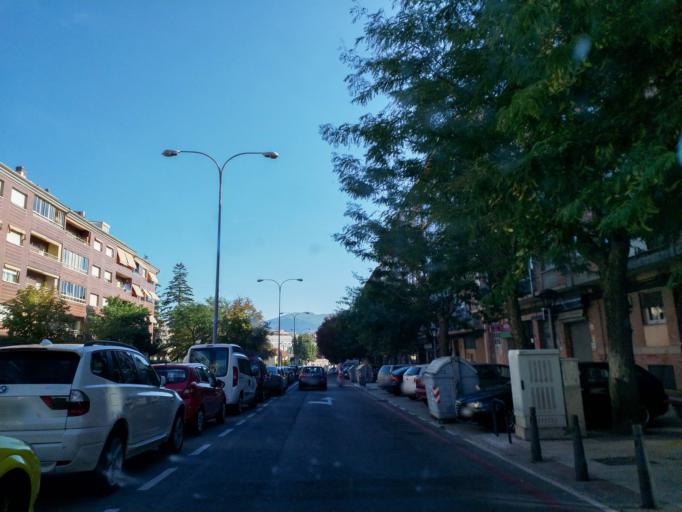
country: ES
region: Castille and Leon
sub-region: Provincia de Segovia
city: Segovia
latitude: 40.9368
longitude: -4.1138
